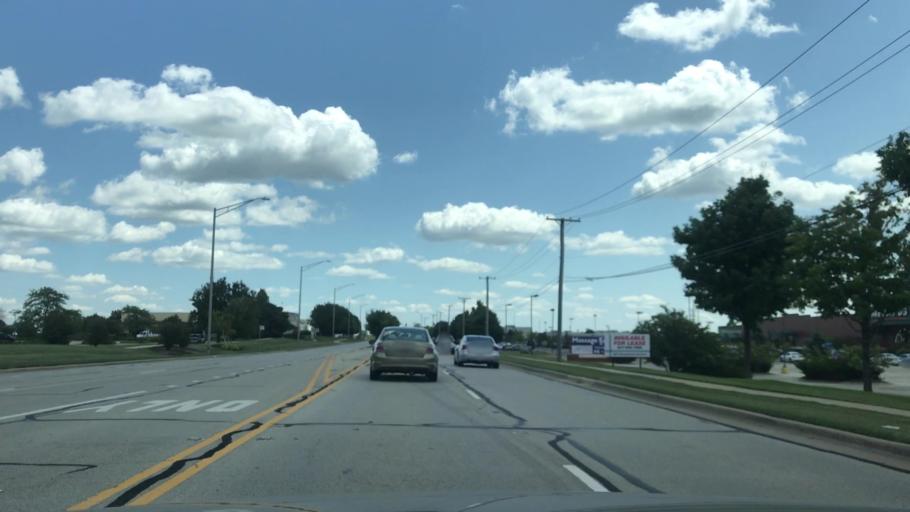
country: US
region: Illinois
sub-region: DuPage County
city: Naperville
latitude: 41.7628
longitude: -88.2004
